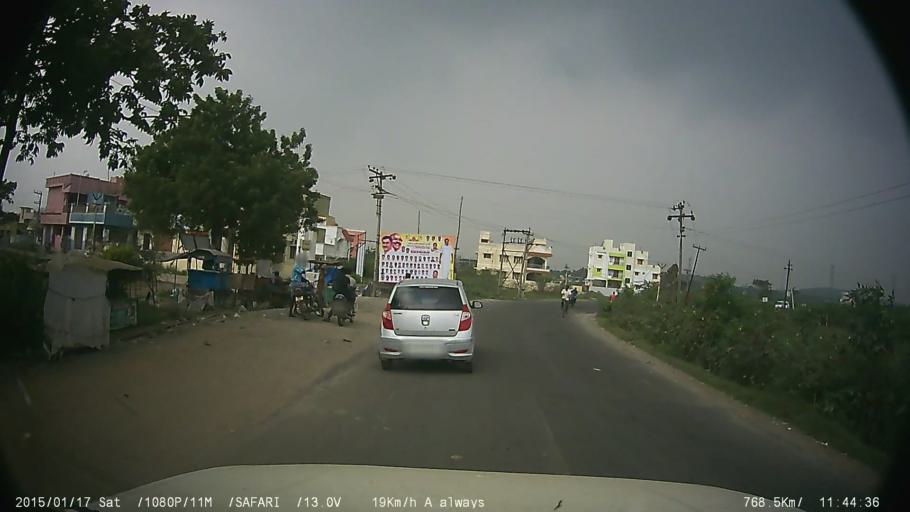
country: IN
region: Tamil Nadu
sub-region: Kancheepuram
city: Singapperumalkovil
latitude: 12.7641
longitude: 80.0017
